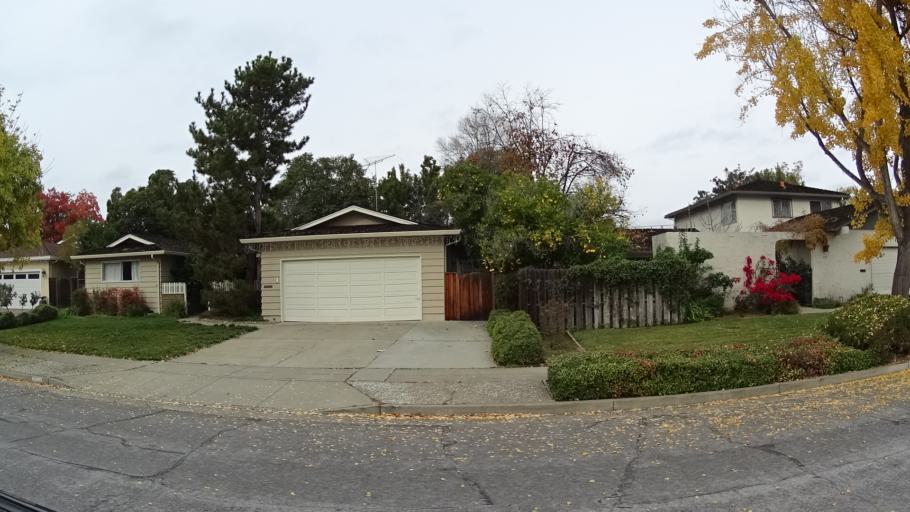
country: US
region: California
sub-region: Santa Clara County
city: Sunnyvale
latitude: 37.3586
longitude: -122.0453
